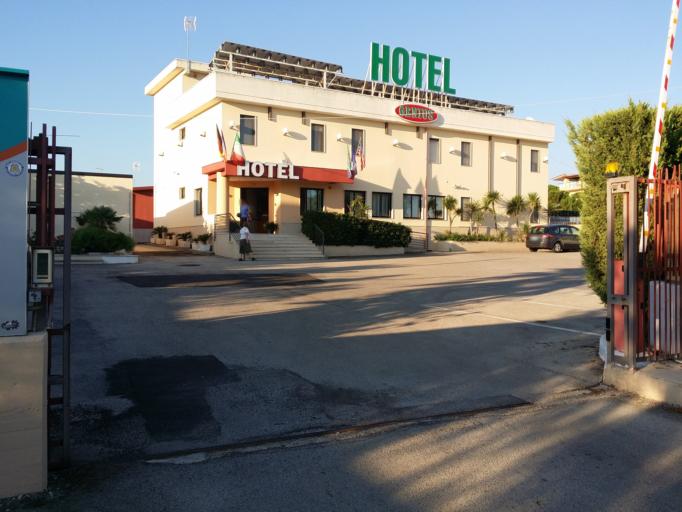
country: IT
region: Apulia
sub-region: Provincia di Bari
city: Corato
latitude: 41.1341
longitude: 16.4175
